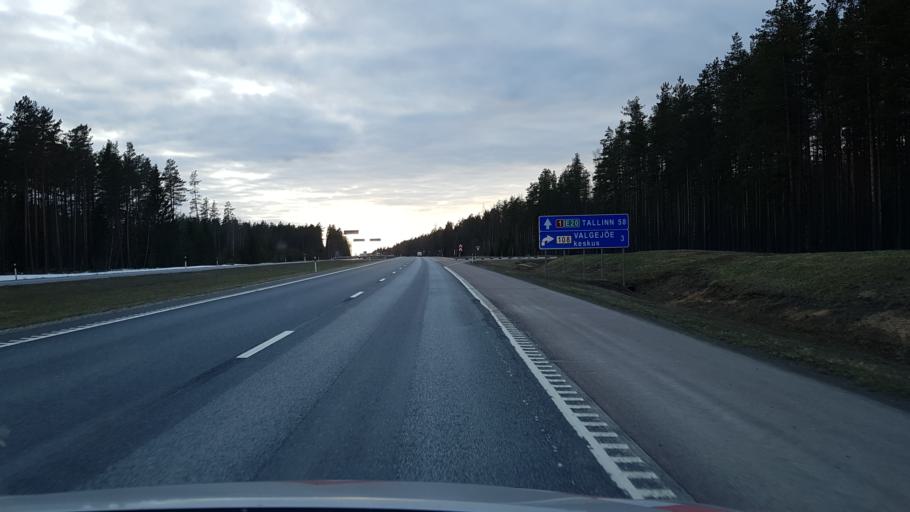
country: EE
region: Harju
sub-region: Loksa linn
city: Loksa
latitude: 59.4639
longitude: 25.7484
